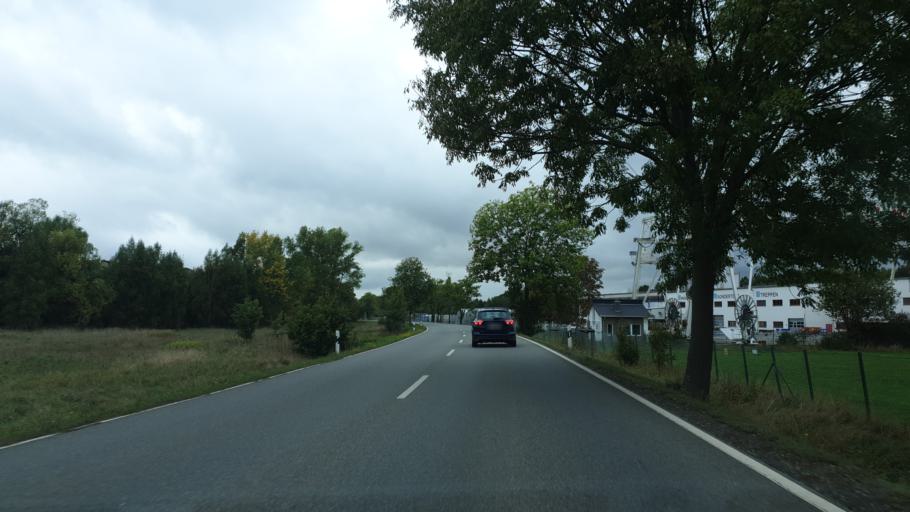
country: DE
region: Saxony
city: Glauchau
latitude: 50.8253
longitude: 12.5612
